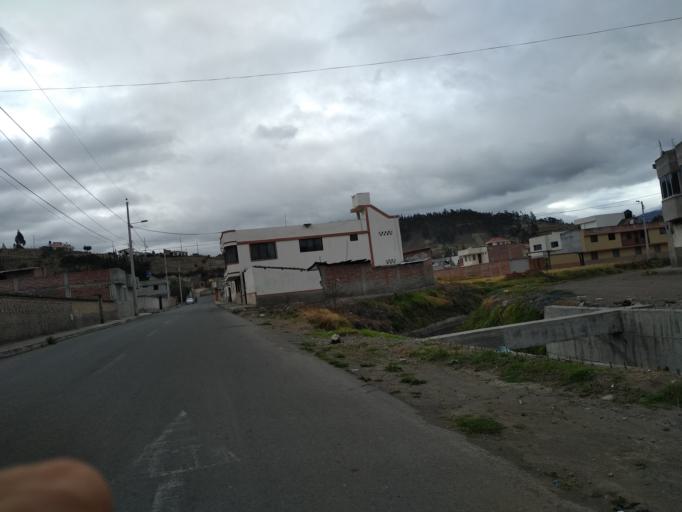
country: EC
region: Chimborazo
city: Riobamba
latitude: -1.6874
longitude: -78.6779
